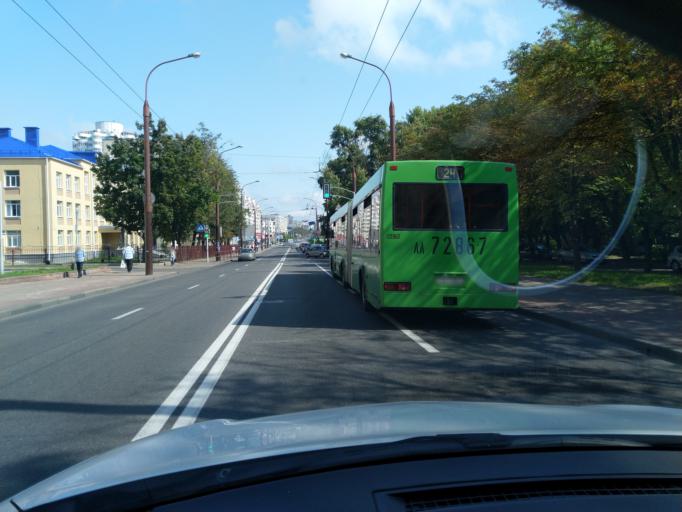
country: BY
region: Minsk
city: Minsk
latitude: 53.9179
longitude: 27.5735
